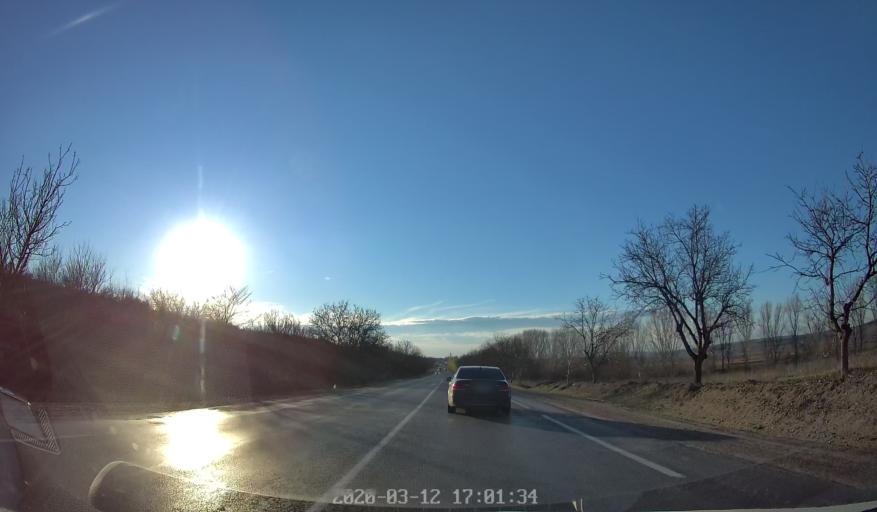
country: MD
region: Anenii Noi
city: Anenii Noi
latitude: 46.8916
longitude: 29.1643
